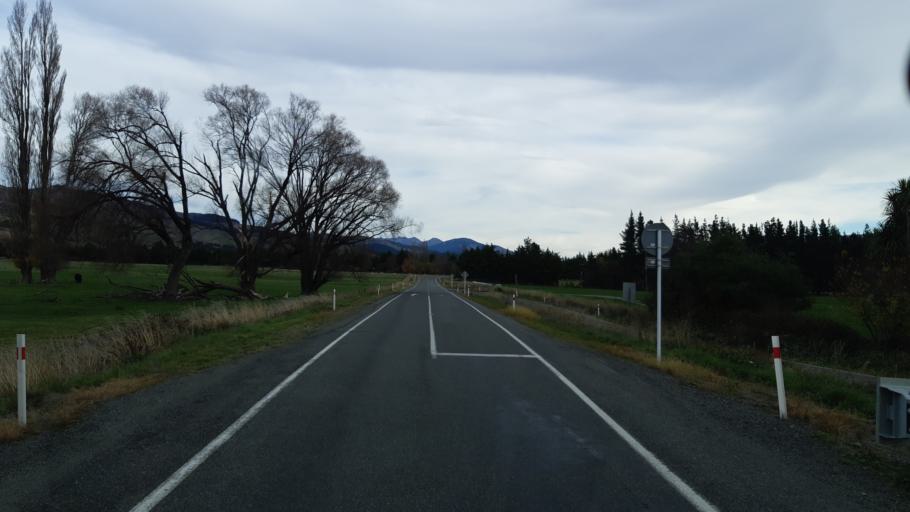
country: NZ
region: Tasman
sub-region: Tasman District
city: Brightwater
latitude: -41.6356
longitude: 173.3234
